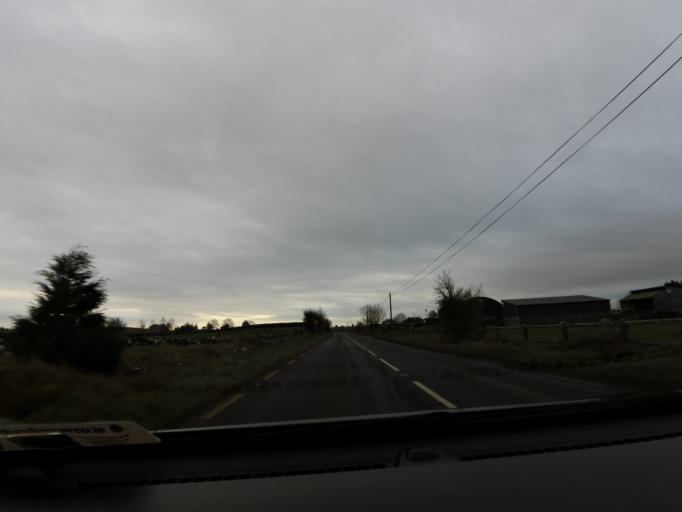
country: IE
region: Connaught
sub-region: County Galway
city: Loughrea
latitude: 53.1972
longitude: -8.4136
